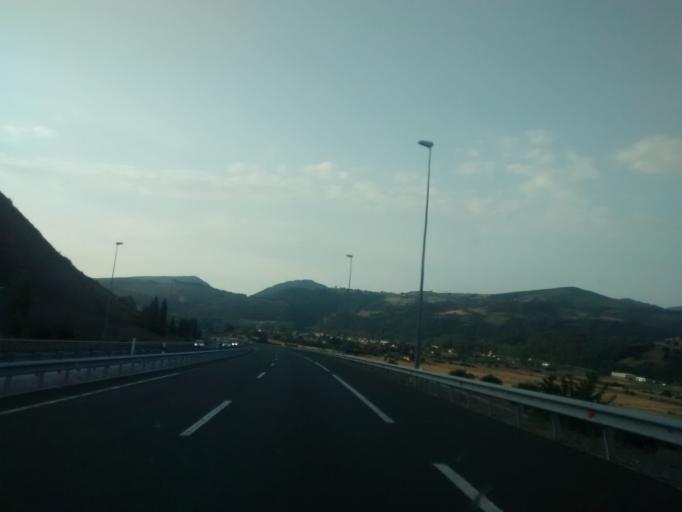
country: ES
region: Cantabria
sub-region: Provincia de Cantabria
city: Arenas de Iguna
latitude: 43.1670
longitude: -4.0525
